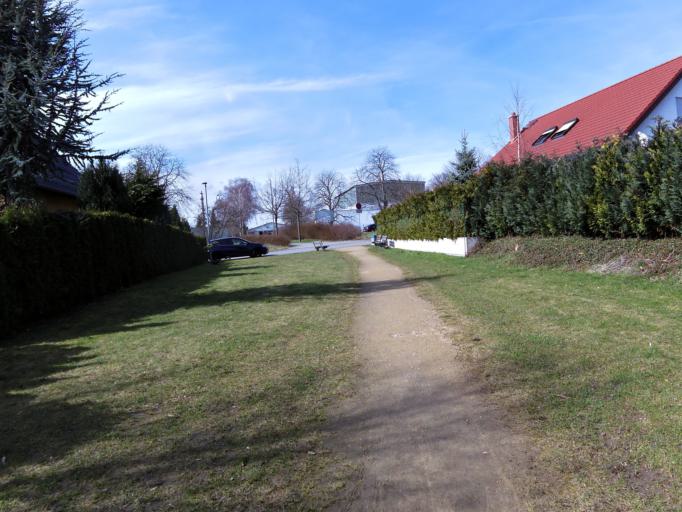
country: DE
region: Saxony
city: Taucha
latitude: 51.3405
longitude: 12.4786
